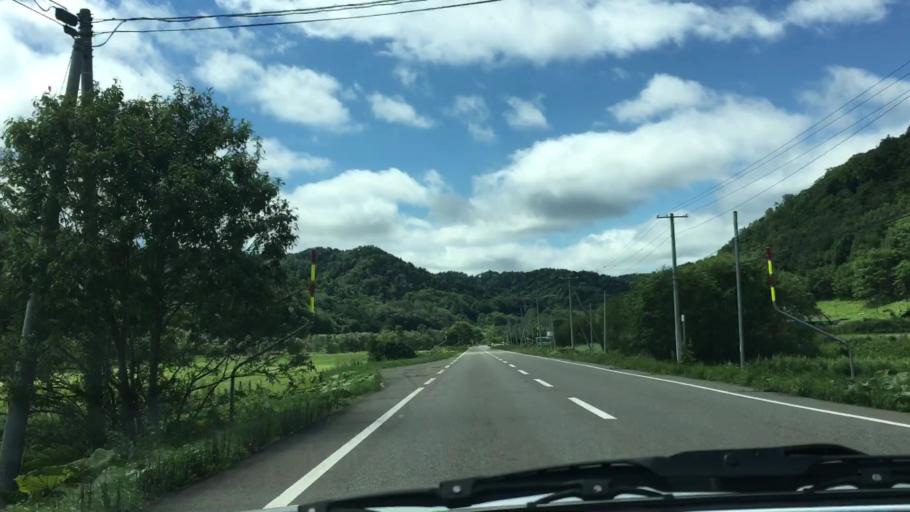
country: JP
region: Hokkaido
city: Kitami
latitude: 43.3648
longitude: 143.8573
